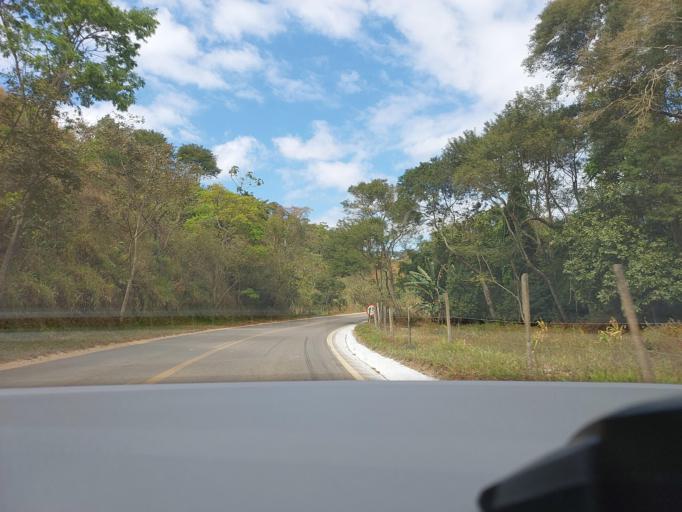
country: BR
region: Minas Gerais
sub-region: Visconde Do Rio Branco
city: Visconde do Rio Branco
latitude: -20.8977
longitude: -42.6537
